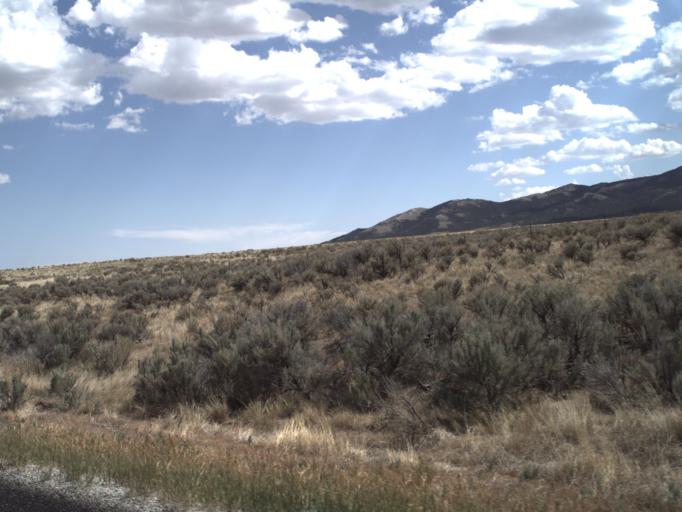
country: US
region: Idaho
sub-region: Minidoka County
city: Rupert
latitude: 41.9884
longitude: -113.1804
